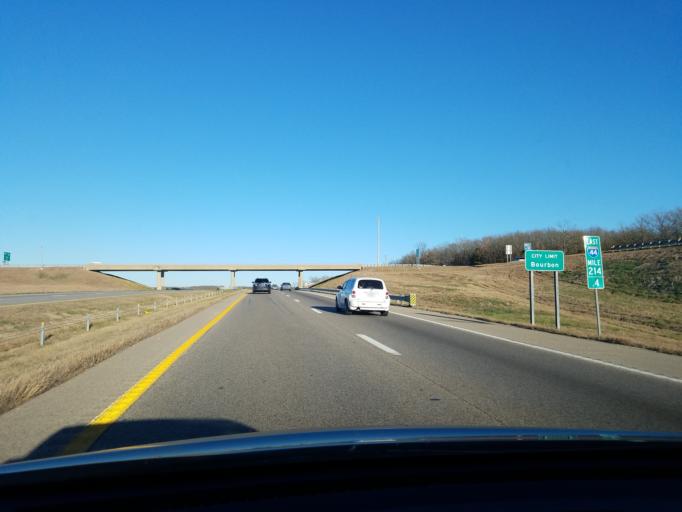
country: US
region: Missouri
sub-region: Crawford County
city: Bourbon
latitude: 38.1193
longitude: -91.3159
